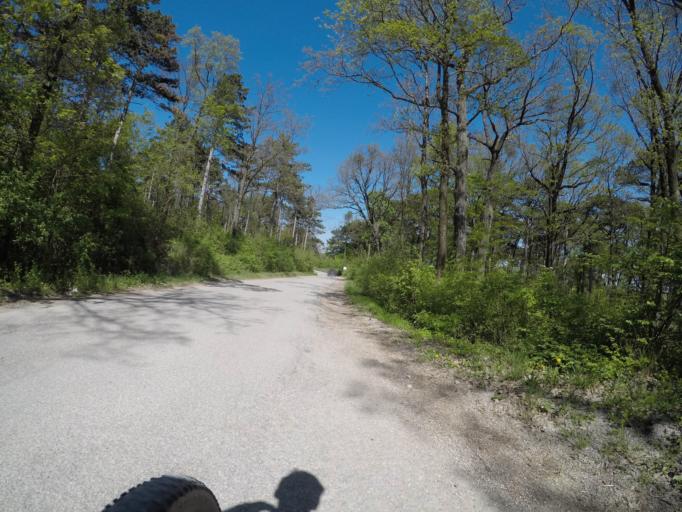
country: AT
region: Lower Austria
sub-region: Politischer Bezirk Modling
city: Gumpoldskirchen
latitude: 48.0568
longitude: 16.2756
